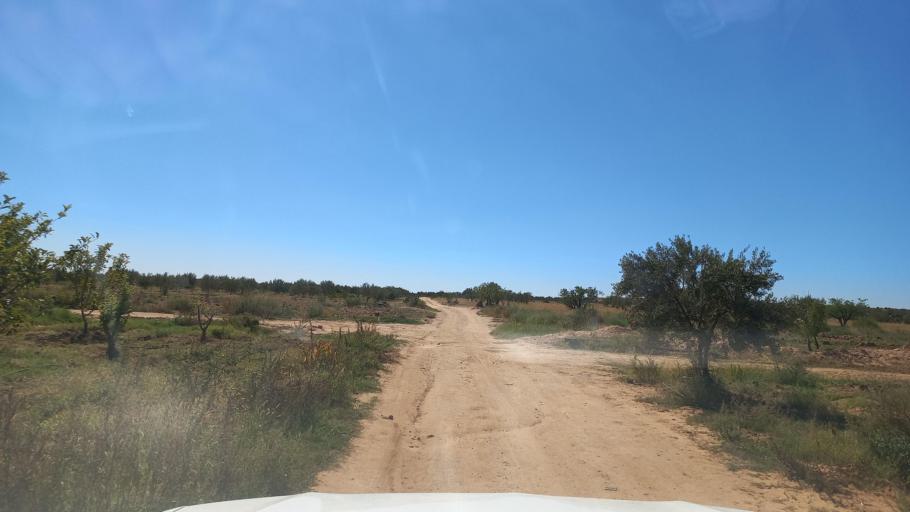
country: TN
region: Al Qasrayn
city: Sbiba
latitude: 35.3617
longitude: 9.0827
